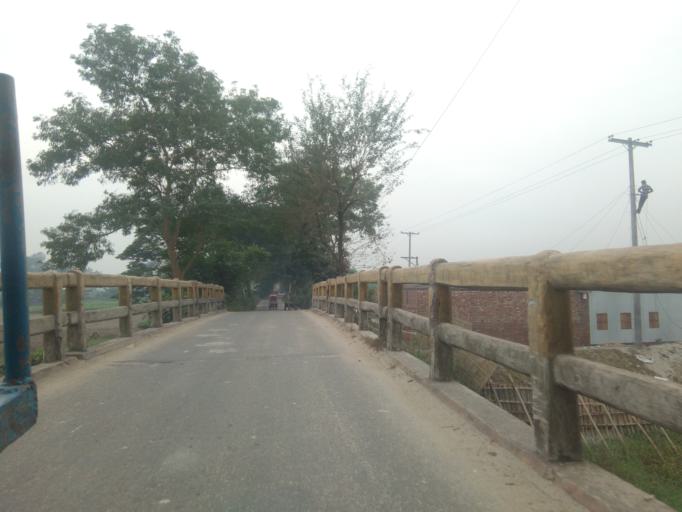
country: BD
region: Dhaka
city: Narayanganj
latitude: 23.5190
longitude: 90.4711
